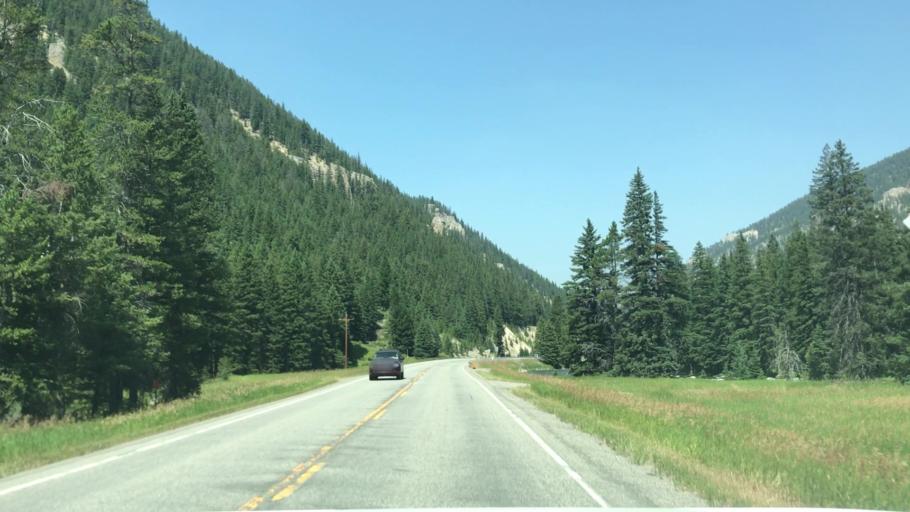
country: US
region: Montana
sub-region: Gallatin County
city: Big Sky
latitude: 45.1262
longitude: -111.2315
